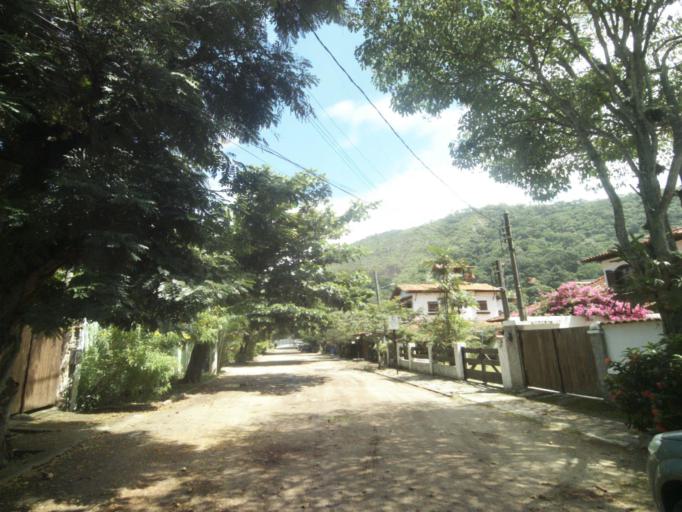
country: BR
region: Rio de Janeiro
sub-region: Niteroi
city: Niteroi
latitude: -22.9719
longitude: -43.0336
